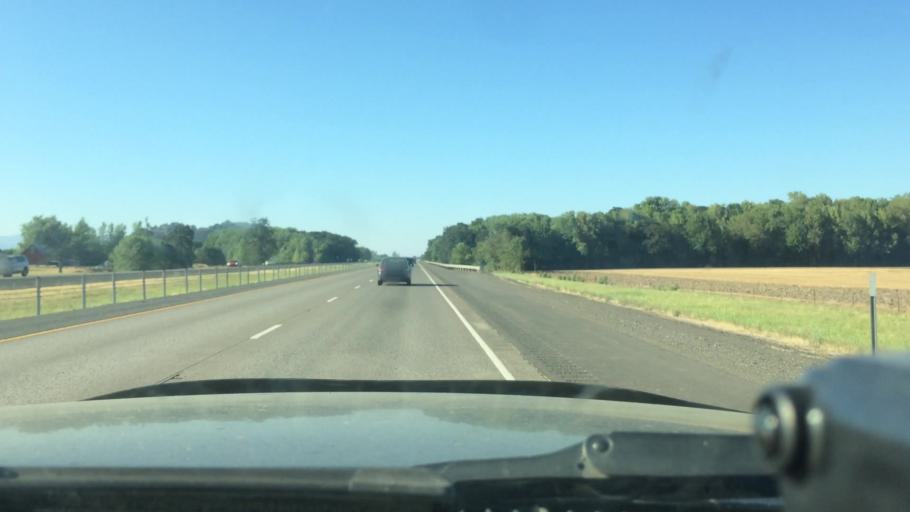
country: US
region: Oregon
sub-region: Linn County
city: Tangent
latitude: 44.4806
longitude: -123.0625
